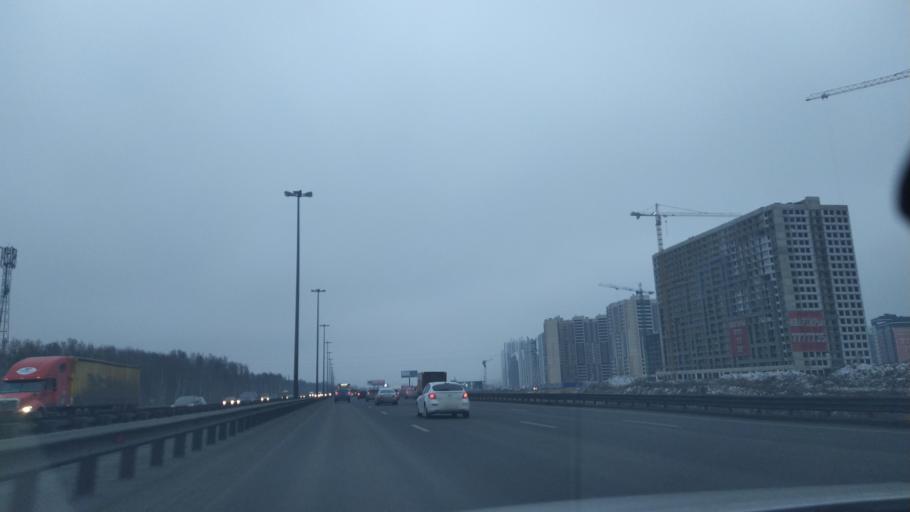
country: RU
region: Leningrad
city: Rybatskoye
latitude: 59.9124
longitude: 30.5258
